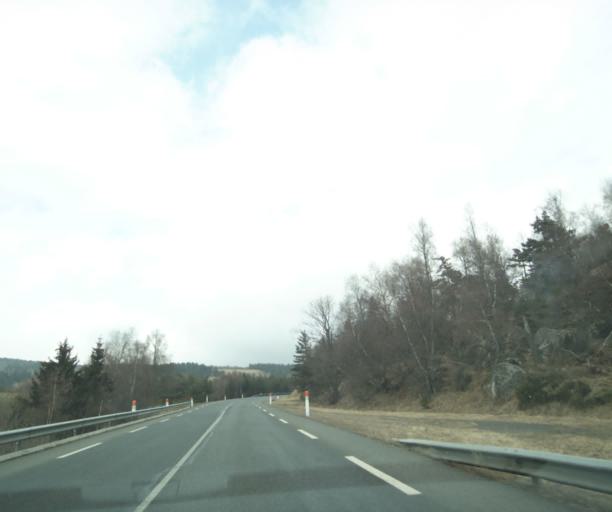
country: FR
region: Languedoc-Roussillon
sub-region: Departement de la Lozere
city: Langogne
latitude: 44.6551
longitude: 3.7411
